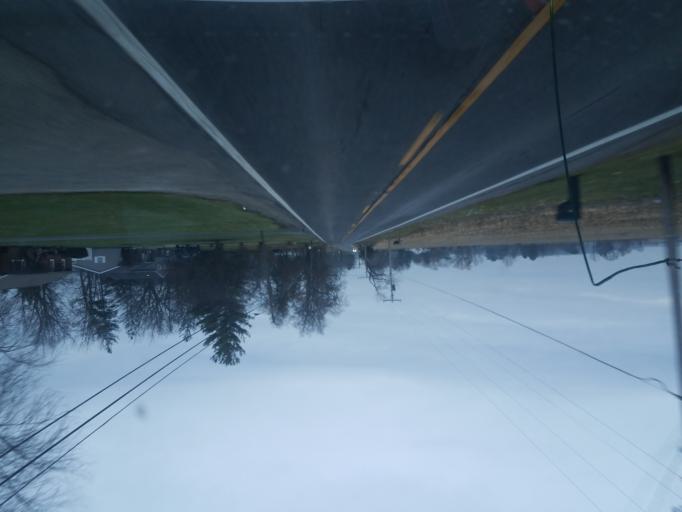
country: US
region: Ohio
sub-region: Marion County
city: Marion
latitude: 40.5584
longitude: -83.0823
